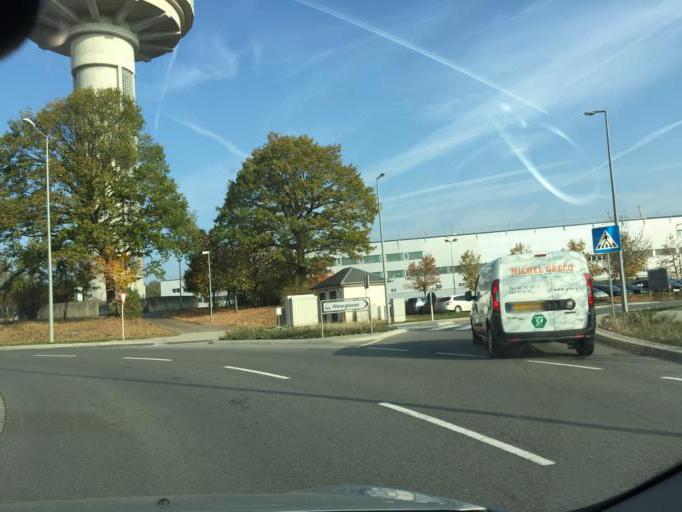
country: LU
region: Luxembourg
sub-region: Canton de Luxembourg
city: Sandweiler
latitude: 49.5963
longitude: 6.2141
